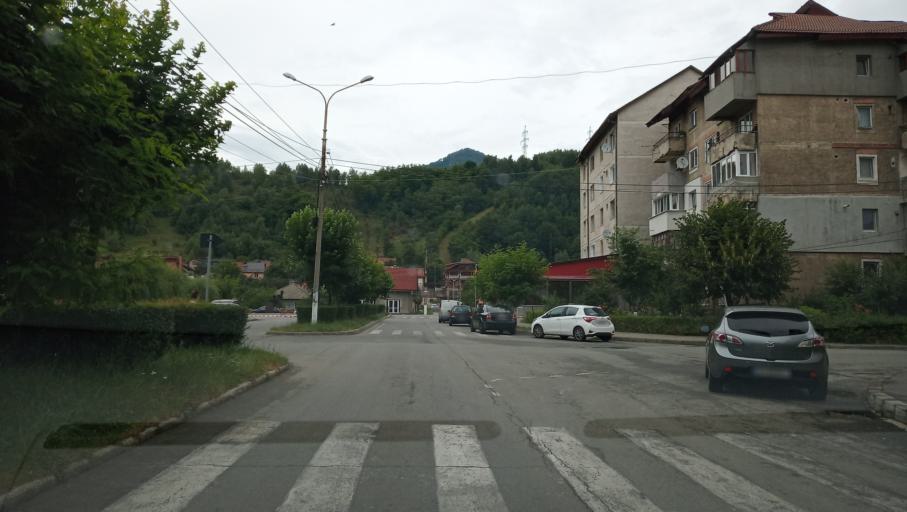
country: RO
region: Hunedoara
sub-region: Municipiul Petrosani
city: Petrosani
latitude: 45.4412
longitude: 23.3736
